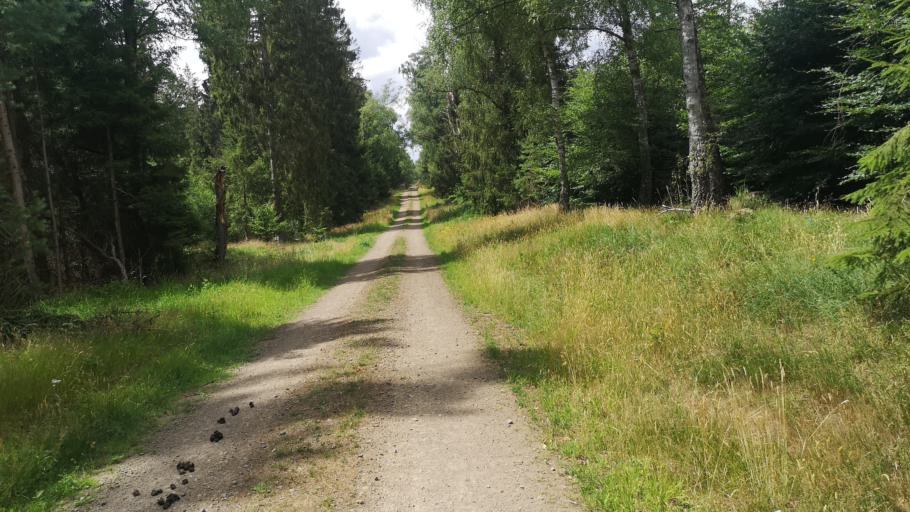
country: DE
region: Lower Saxony
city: Dahlem
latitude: 53.2361
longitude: 10.7198
